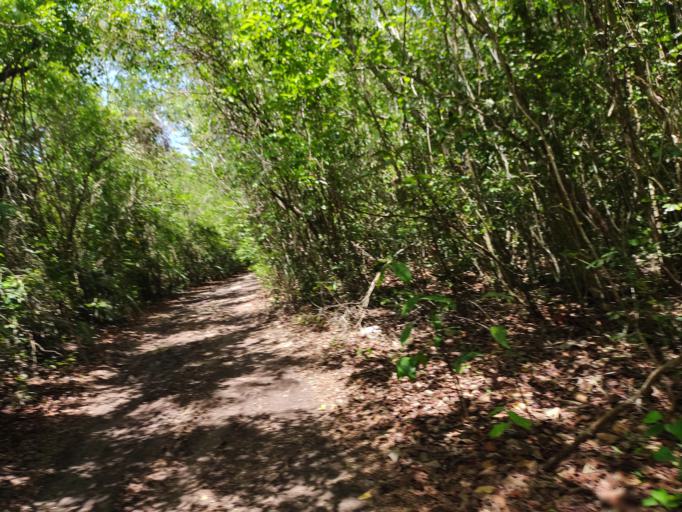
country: MX
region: Quintana Roo
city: San Miguel de Cozumel
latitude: 20.5064
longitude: -86.8907
